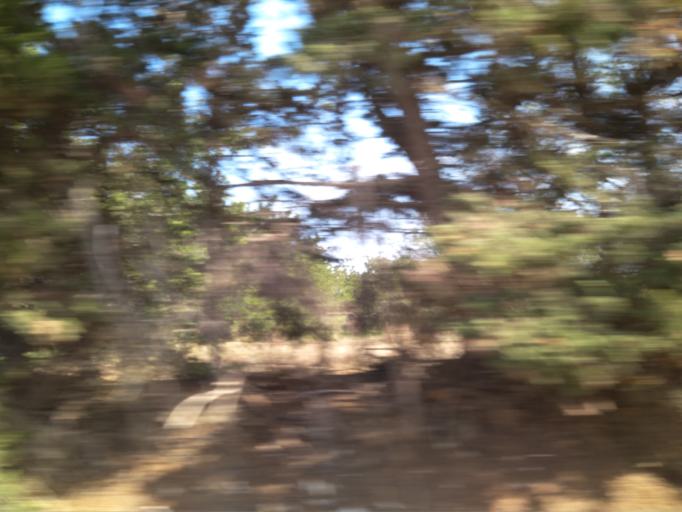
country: PT
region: Faro
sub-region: Faro
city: Santa Barbara de Nexe
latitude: 37.0632
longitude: -7.9550
